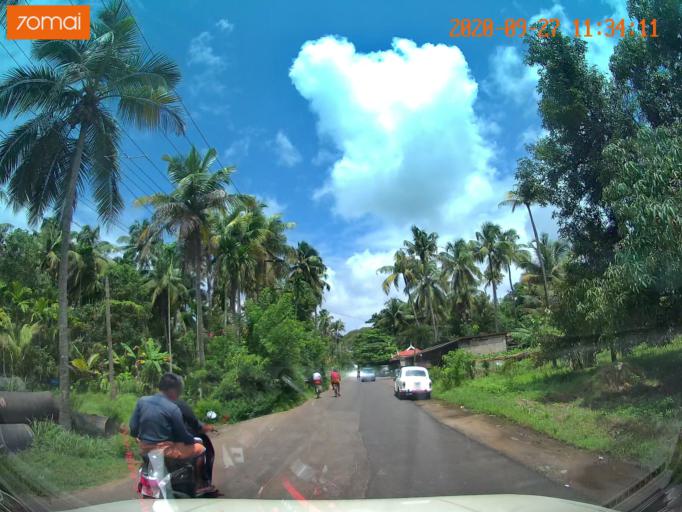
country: IN
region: Kerala
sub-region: Thrissur District
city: Thanniyam
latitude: 10.4356
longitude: 76.1272
